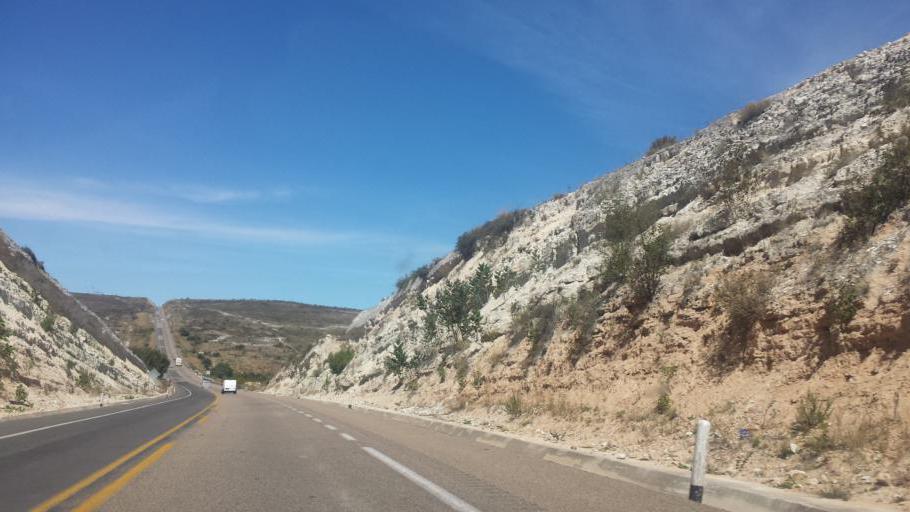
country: MX
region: Oaxaca
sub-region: Villa Tejupam de la Union
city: Villa Tejupam de la Union
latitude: 17.7621
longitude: -97.3554
